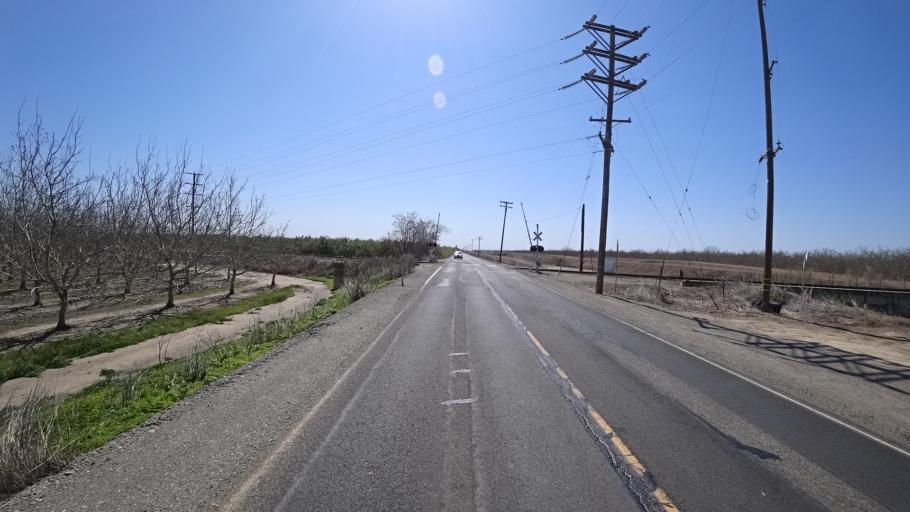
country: US
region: California
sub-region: Glenn County
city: Hamilton City
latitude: 39.7561
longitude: -122.0250
